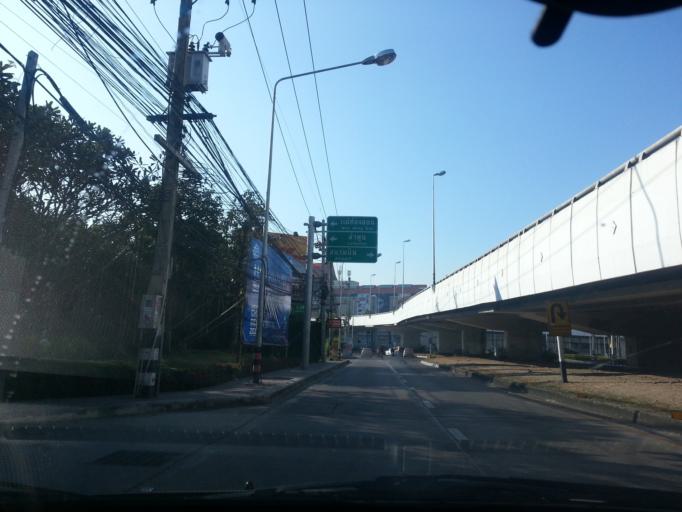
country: TH
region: Chiang Mai
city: Chiang Mai
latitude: 18.7714
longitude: 98.9761
